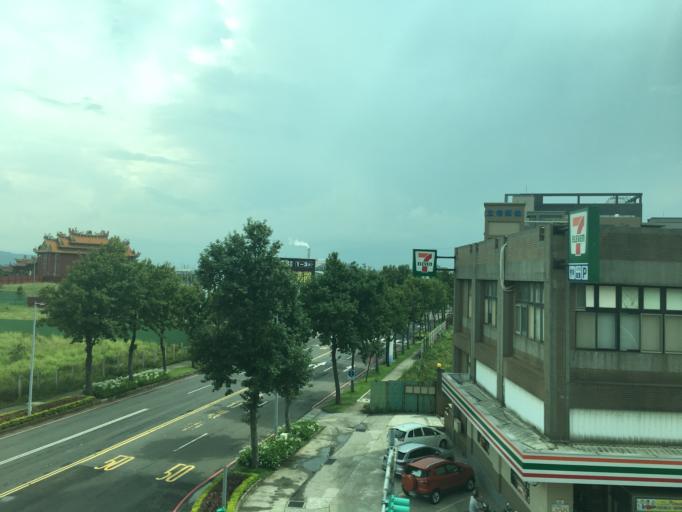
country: TW
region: Taiwan
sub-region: Taoyuan
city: Taoyuan
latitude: 25.0502
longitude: 121.3817
